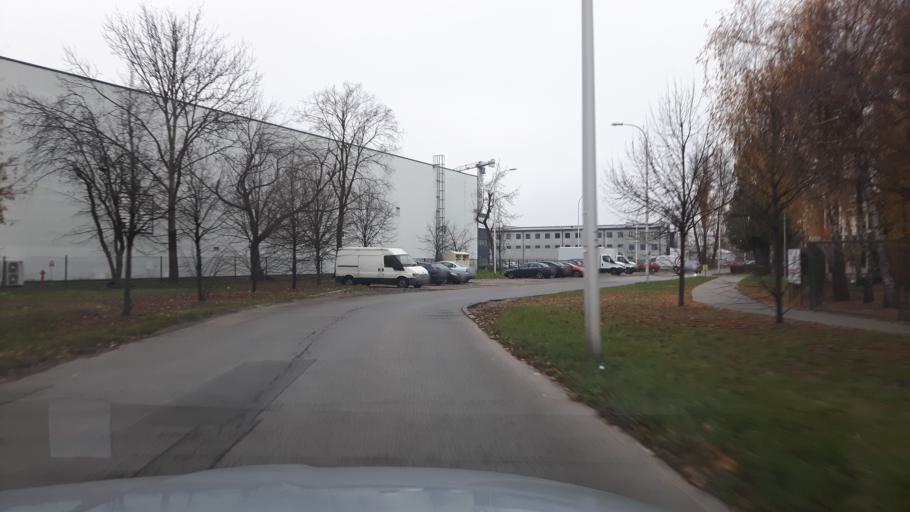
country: PL
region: Masovian Voivodeship
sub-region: Warszawa
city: Praga Poludnie
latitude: 52.2719
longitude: 21.0767
